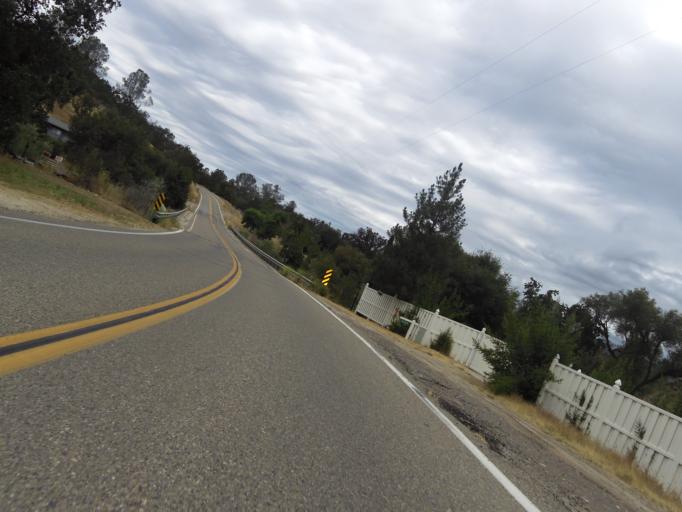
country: US
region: California
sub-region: Madera County
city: Yosemite Lakes
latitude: 37.2365
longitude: -119.7747
